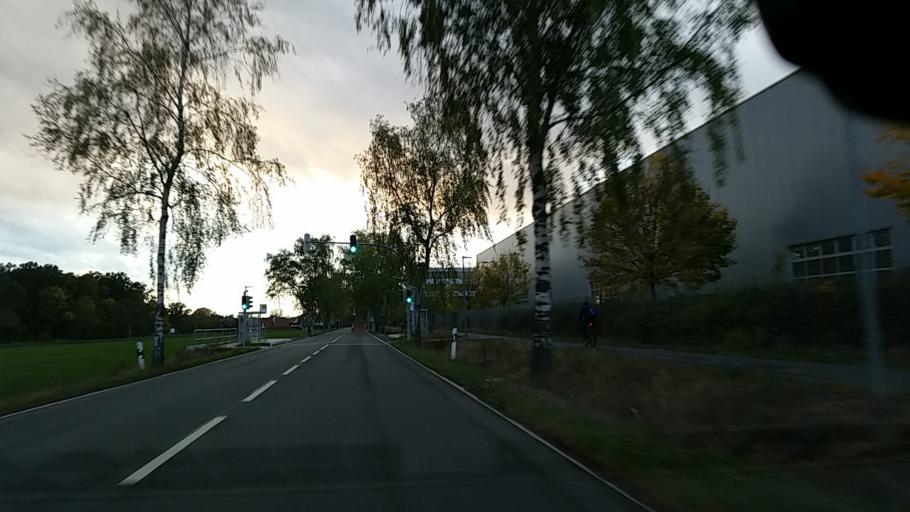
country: DE
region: Lower Saxony
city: Tappenbeck
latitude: 52.4527
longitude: 10.7590
